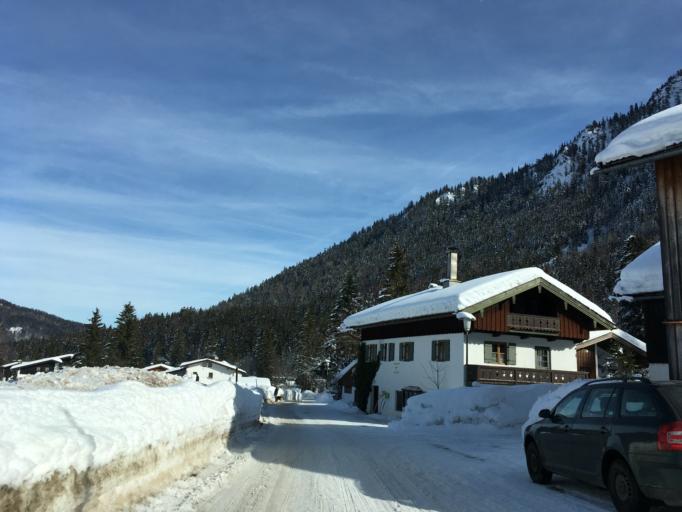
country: DE
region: Bavaria
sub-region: Upper Bavaria
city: Schliersee
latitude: 47.6915
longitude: 11.8863
